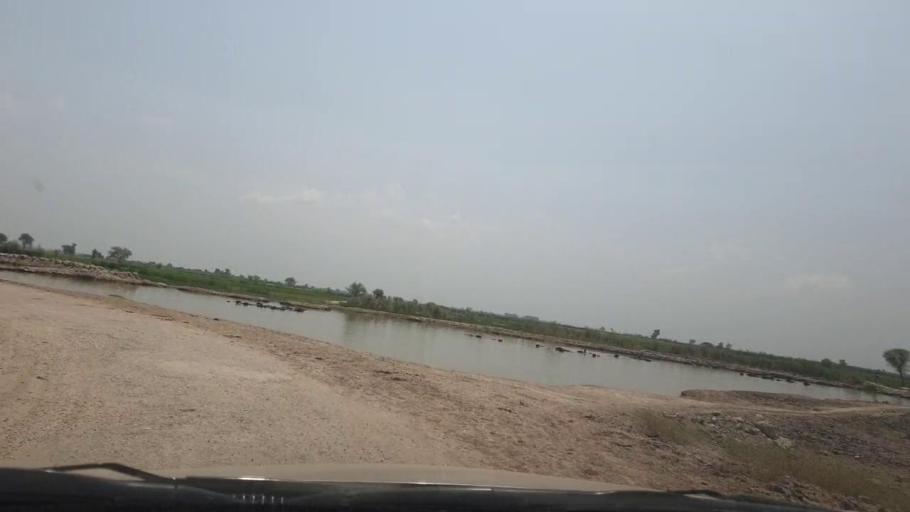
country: PK
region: Sindh
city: Ratodero
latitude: 27.7221
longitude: 68.2875
